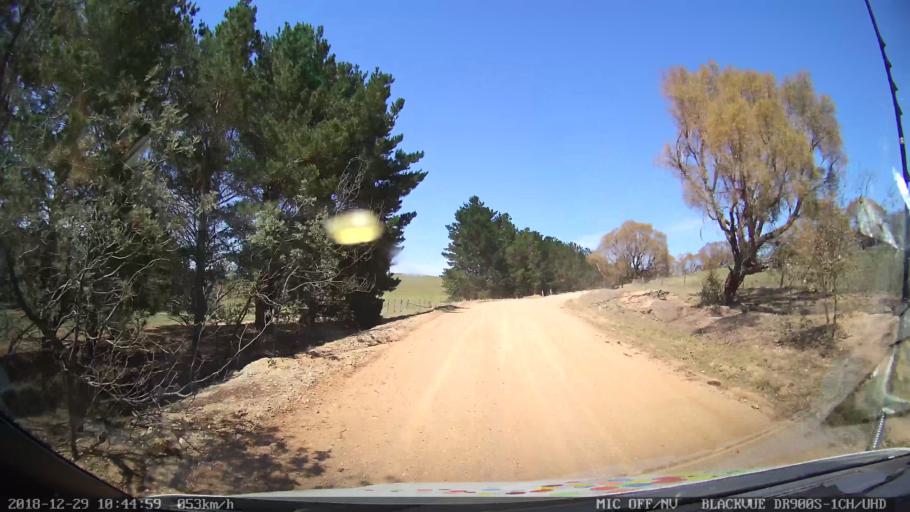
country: AU
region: New South Wales
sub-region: Palerang
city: Bungendore
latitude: -35.0449
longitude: 149.5247
